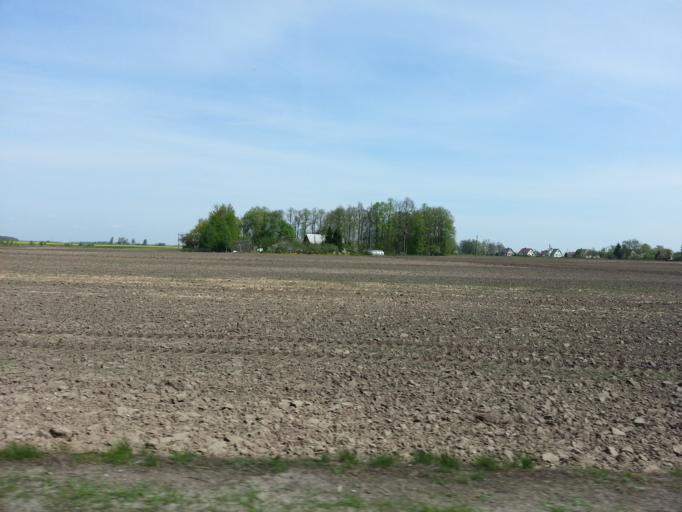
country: LT
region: Panevezys
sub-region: Panevezys City
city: Panevezys
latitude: 55.8682
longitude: 24.2389
